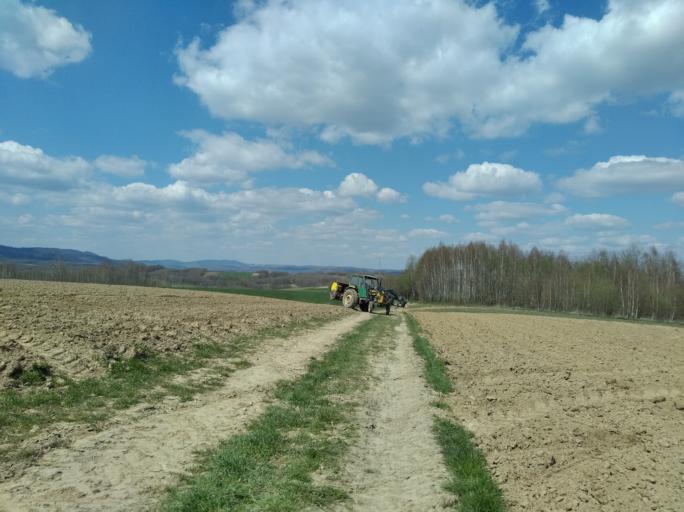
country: PL
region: Subcarpathian Voivodeship
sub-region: Powiat strzyzowski
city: Wysoka Strzyzowska
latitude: 49.8415
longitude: 21.7621
